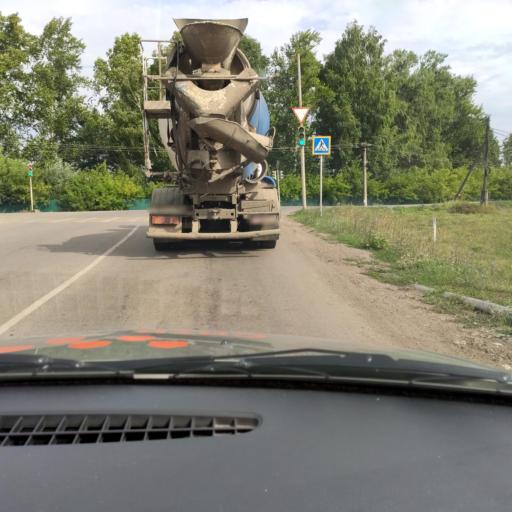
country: RU
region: Bashkortostan
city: Iglino
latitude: 54.8505
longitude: 56.4517
